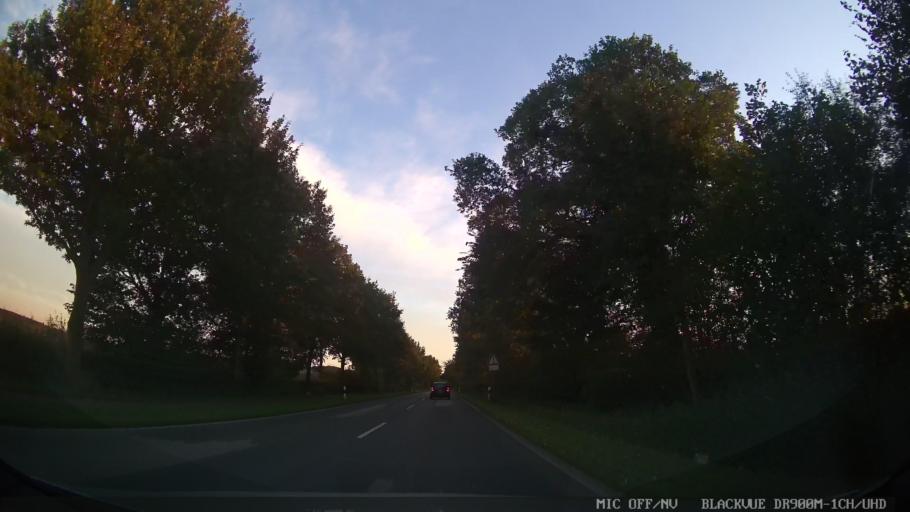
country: DE
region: Schleswig-Holstein
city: Susel
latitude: 54.0334
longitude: 10.6819
